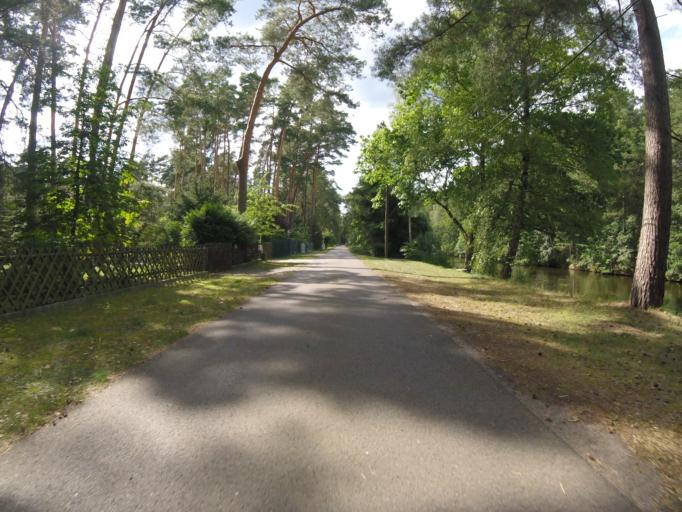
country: DE
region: Brandenburg
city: Halbe
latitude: 52.0968
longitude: 13.7805
